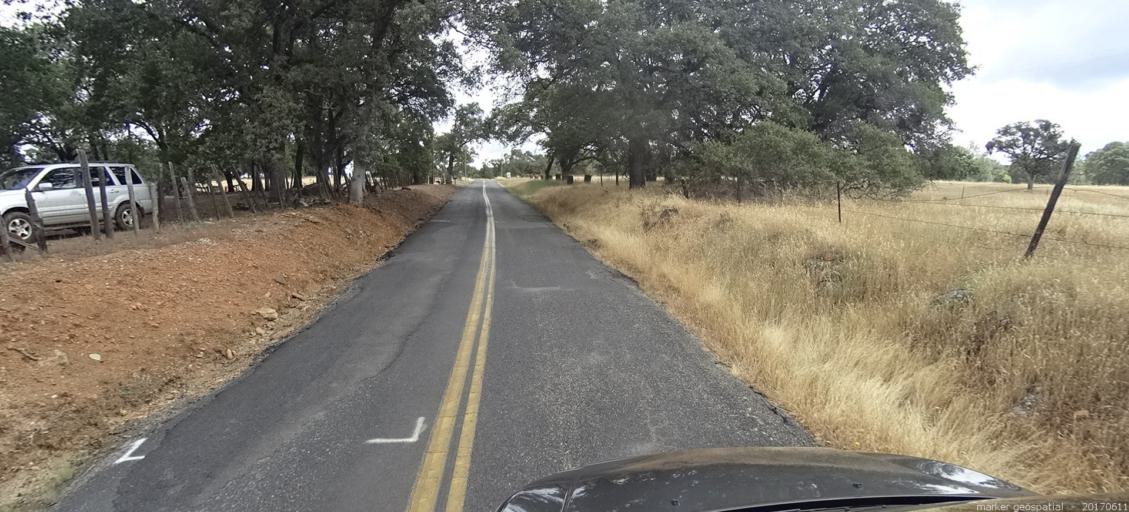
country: US
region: California
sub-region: Butte County
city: Oroville
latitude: 39.6033
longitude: -121.5332
